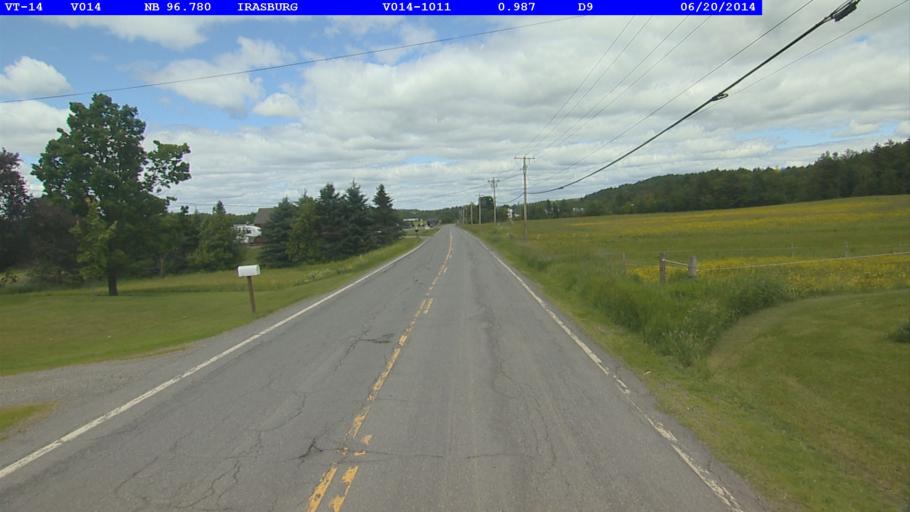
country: US
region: Vermont
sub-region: Orleans County
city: Newport
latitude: 44.7852
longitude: -72.3021
